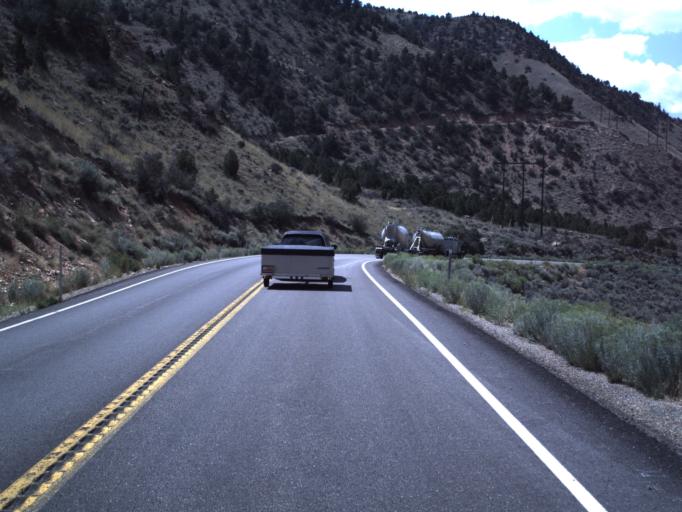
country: US
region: Utah
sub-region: Carbon County
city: Helper
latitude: 39.7327
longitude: -110.8501
